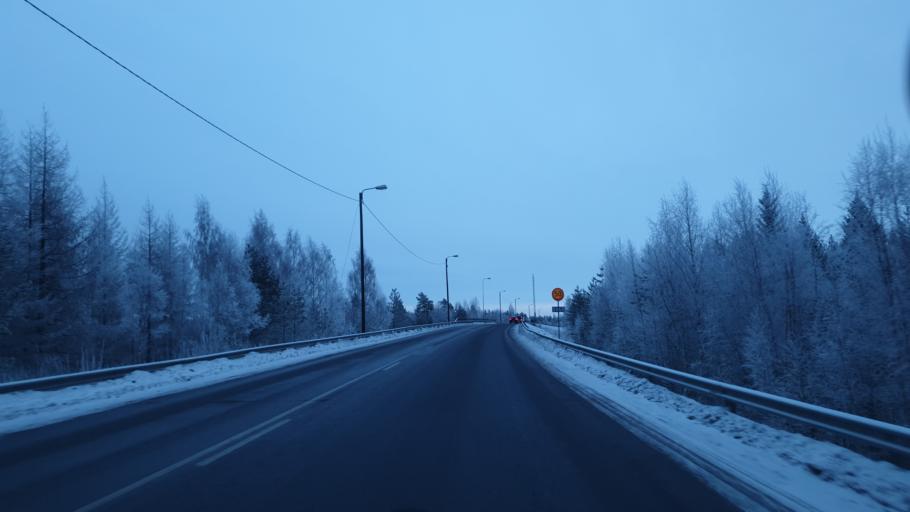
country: FI
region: Northern Ostrobothnia
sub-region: Oulu
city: Haukipudas
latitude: 65.2004
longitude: 25.4210
